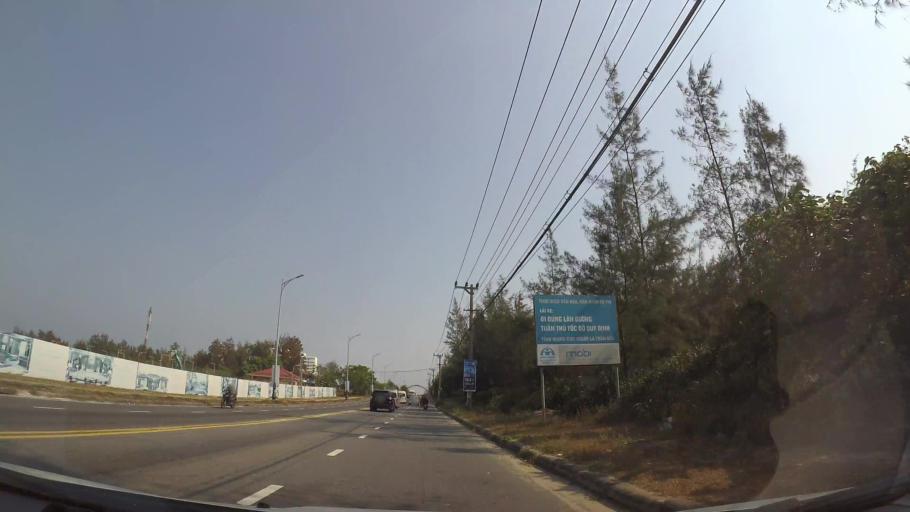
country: VN
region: Da Nang
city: Ngu Hanh Son
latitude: 15.9713
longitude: 108.2818
